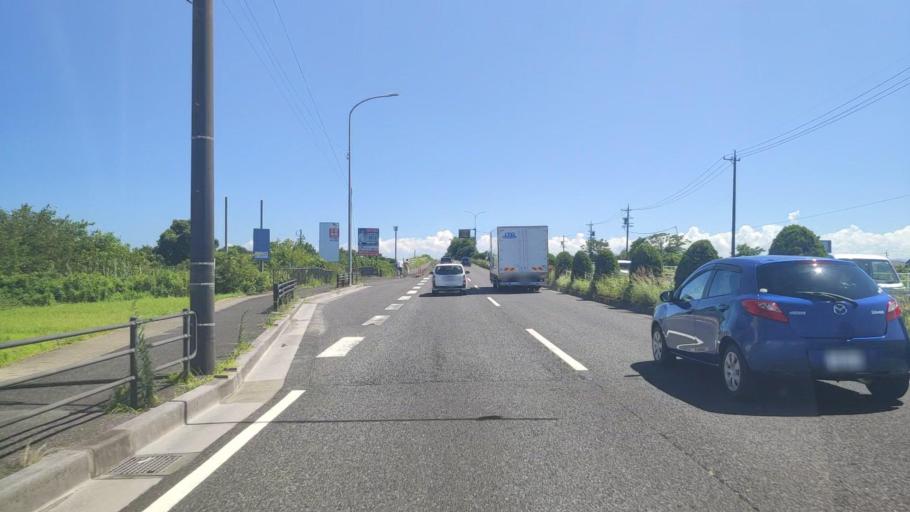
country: JP
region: Mie
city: Tsu-shi
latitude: 34.7657
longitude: 136.5257
